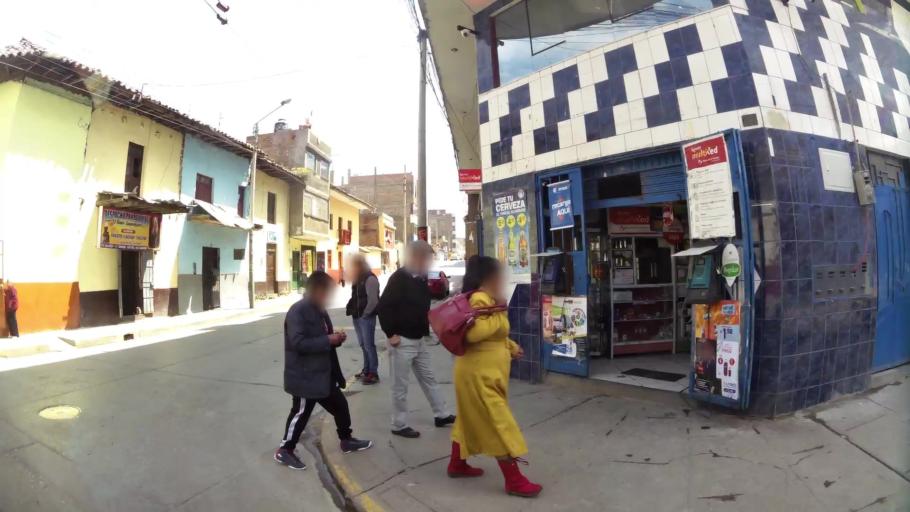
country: PE
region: Junin
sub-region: Provincia de Huancayo
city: El Tambo
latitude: -12.0715
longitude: -75.2118
